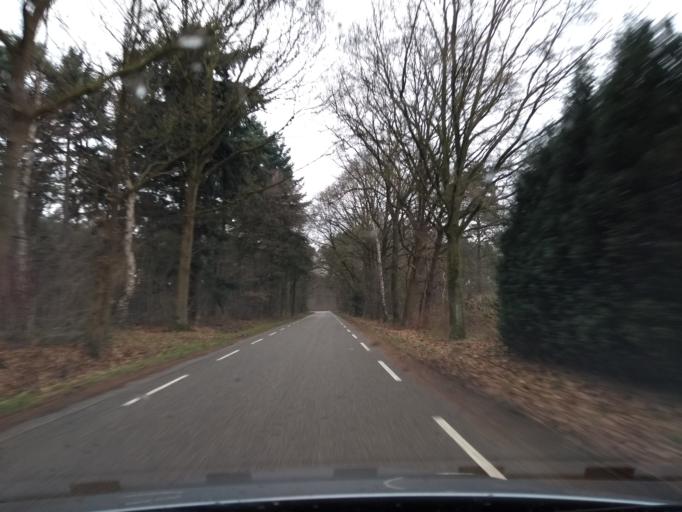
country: NL
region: Gelderland
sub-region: Gemeente Bronckhorst
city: Zelhem
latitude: 52.0496
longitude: 6.4069
